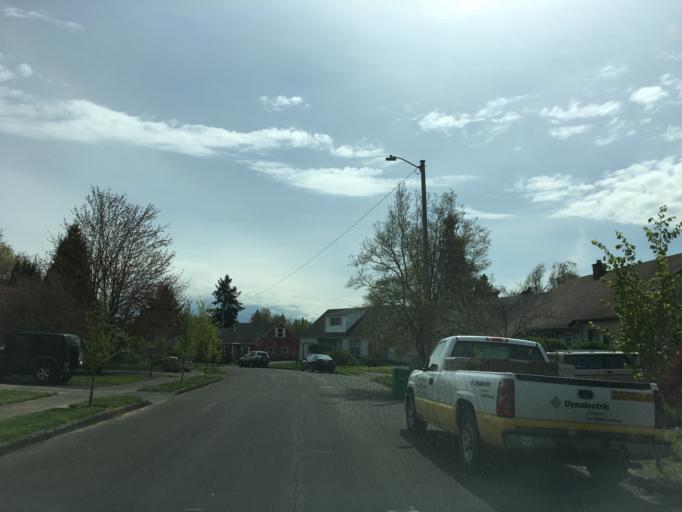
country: US
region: Oregon
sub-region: Multnomah County
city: Lents
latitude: 45.5457
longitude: -122.5730
